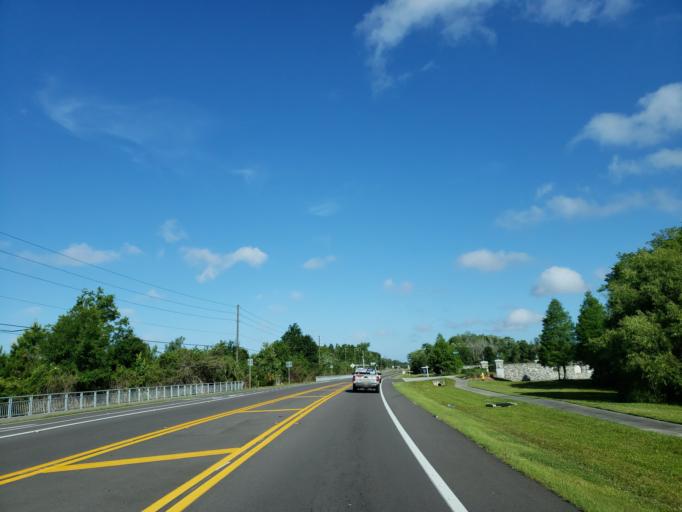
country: US
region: Florida
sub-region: Pinellas County
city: East Lake
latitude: 28.1457
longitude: -82.6882
